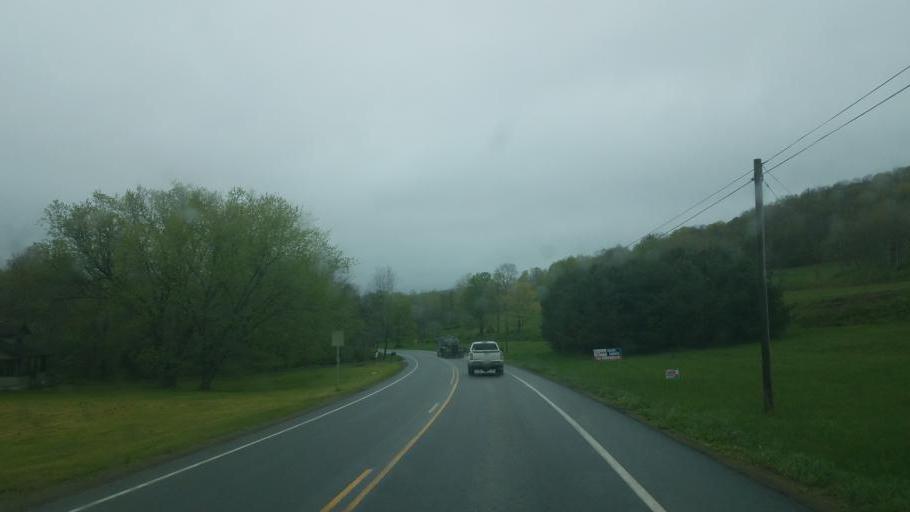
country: US
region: Pennsylvania
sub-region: McKean County
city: Smethport
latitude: 41.8169
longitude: -78.4020
